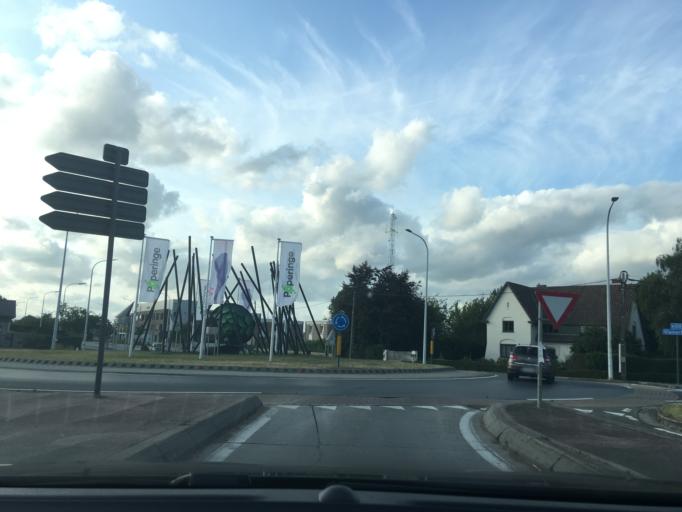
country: BE
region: Flanders
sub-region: Provincie West-Vlaanderen
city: Poperinge
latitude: 50.8545
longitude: 2.7455
